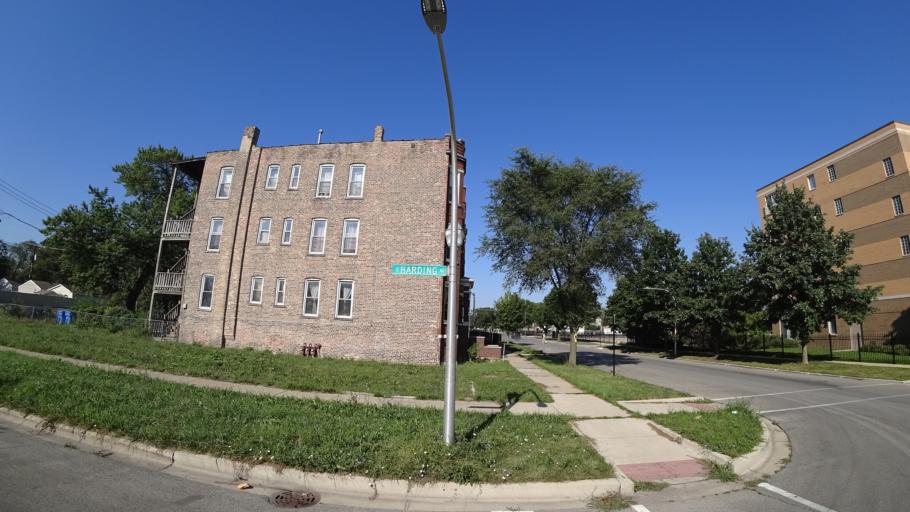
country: US
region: Illinois
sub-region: Cook County
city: Cicero
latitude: 41.8624
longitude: -87.7239
